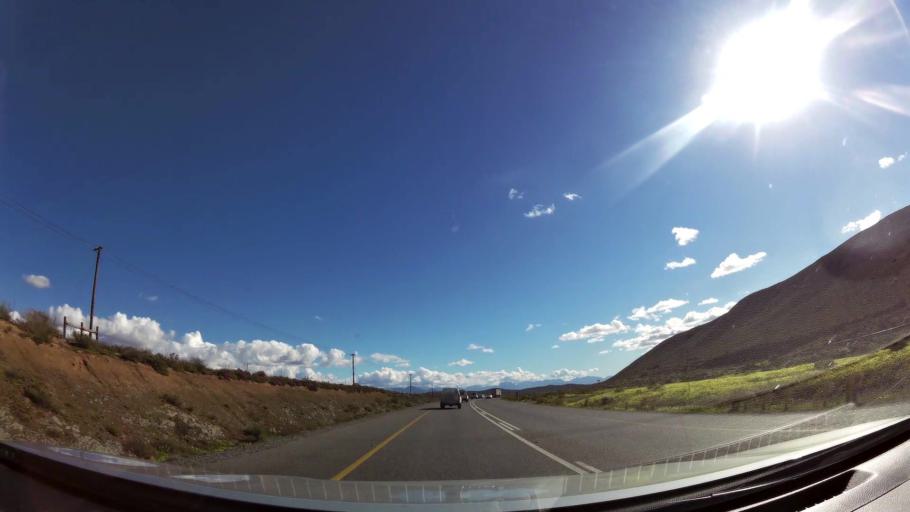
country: ZA
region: Western Cape
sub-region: Cape Winelands District Municipality
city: Worcester
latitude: -33.7349
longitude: 19.6570
